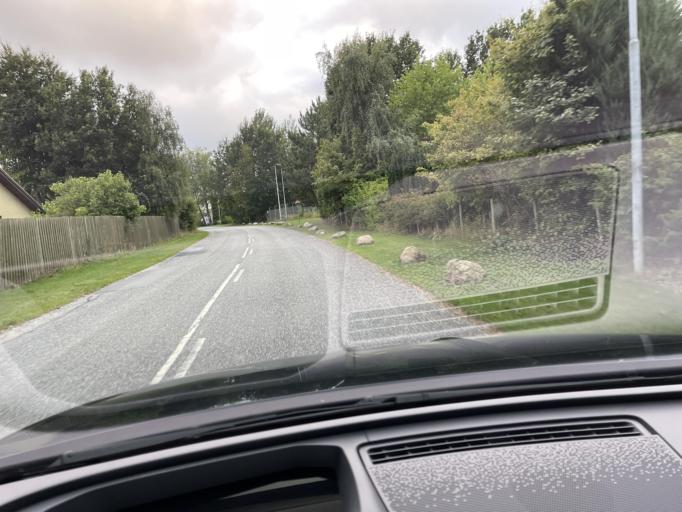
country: DK
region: Zealand
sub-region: Solrod Kommune
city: Havdrup
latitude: 55.5525
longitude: 12.1226
